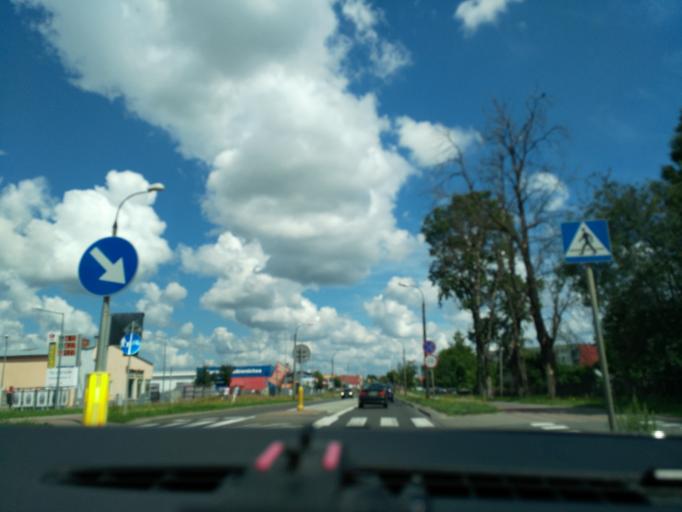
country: PL
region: Podlasie
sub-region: Powiat bielski
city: Bielsk Podlaski
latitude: 52.7722
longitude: 23.1843
